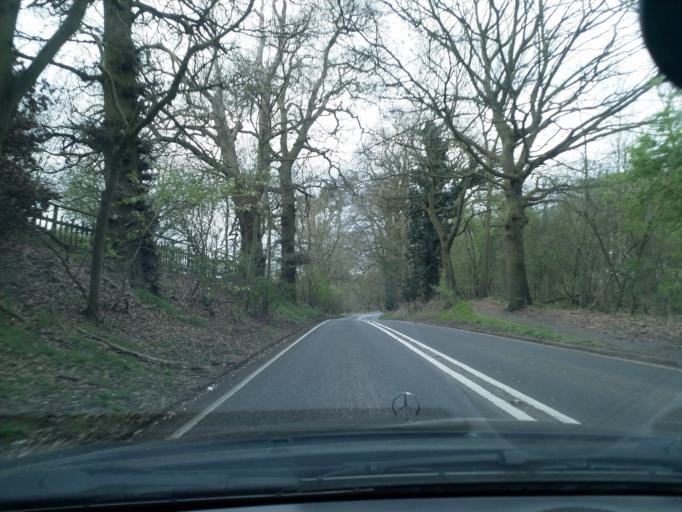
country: GB
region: England
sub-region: Warwickshire
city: Royal Leamington Spa
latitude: 52.3482
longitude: -1.5144
